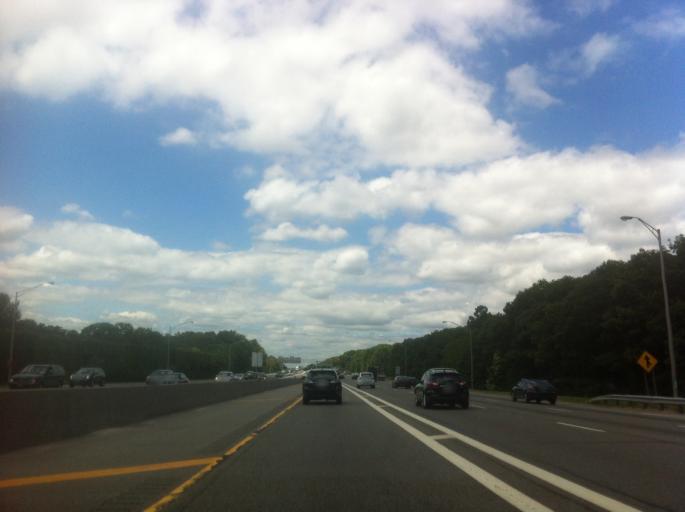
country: US
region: New York
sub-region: Suffolk County
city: Ronkonkoma
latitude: 40.8123
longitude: -73.1281
